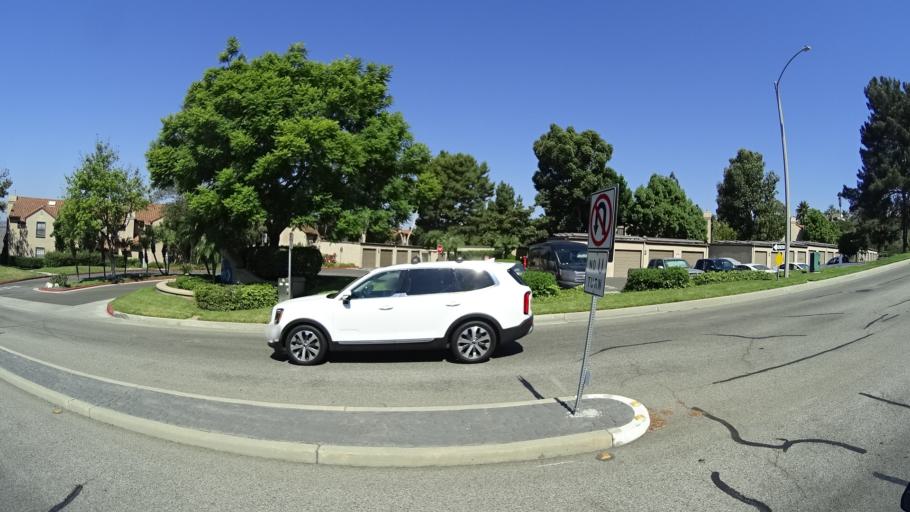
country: US
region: California
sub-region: Orange County
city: San Clemente
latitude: 33.4448
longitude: -117.5993
